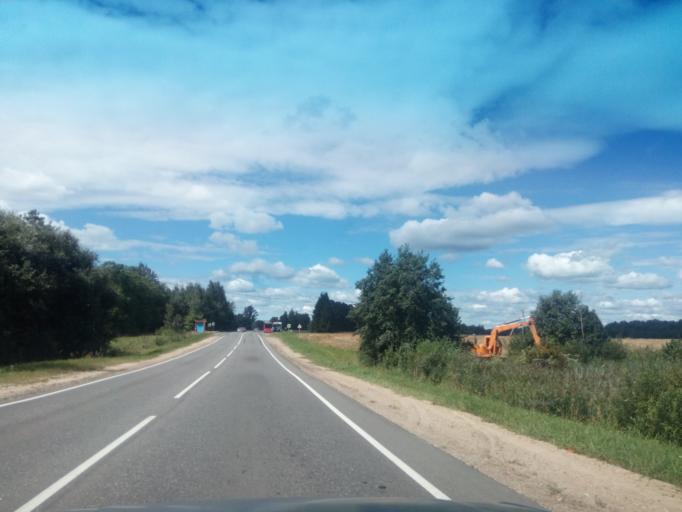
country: BY
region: Vitebsk
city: Polatsk
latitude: 55.5059
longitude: 28.7260
